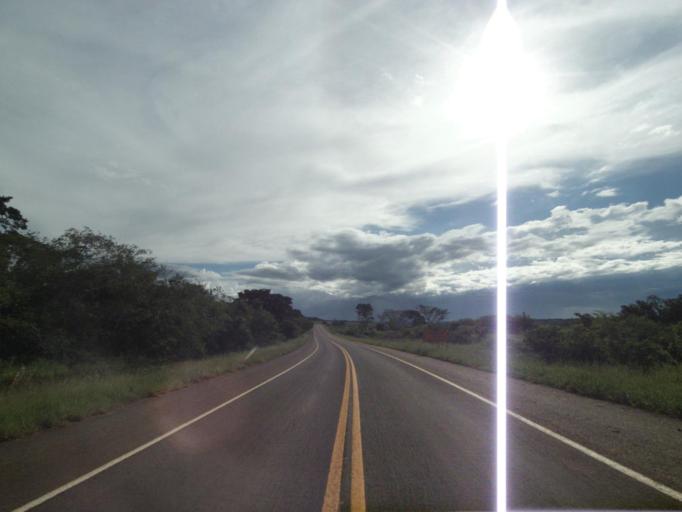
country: BR
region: Goias
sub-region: Jaragua
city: Jaragua
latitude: -15.8929
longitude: -49.5172
